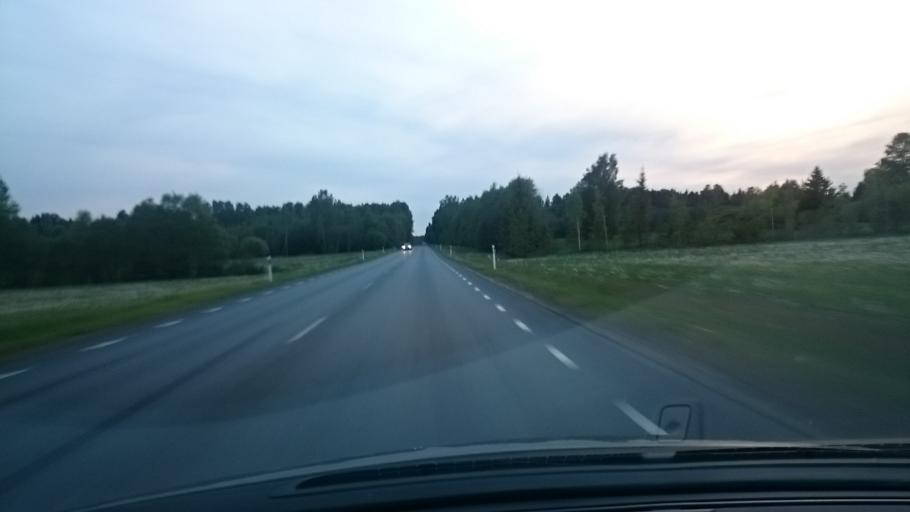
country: EE
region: Raplamaa
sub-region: Kehtna vald
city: Kehtna
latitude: 58.8502
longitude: 25.0269
